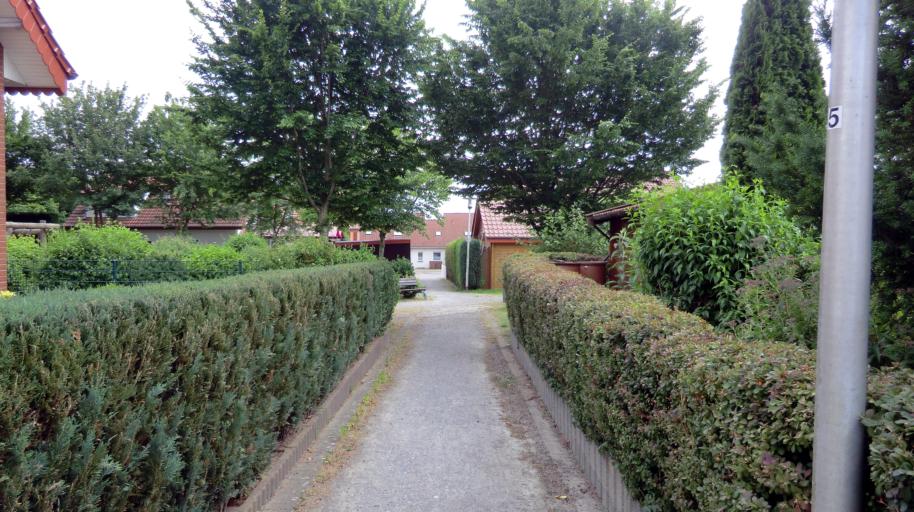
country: DE
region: North Rhine-Westphalia
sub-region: Regierungsbezirk Detmold
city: Hiddenhausen
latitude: 52.1553
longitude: 8.6418
